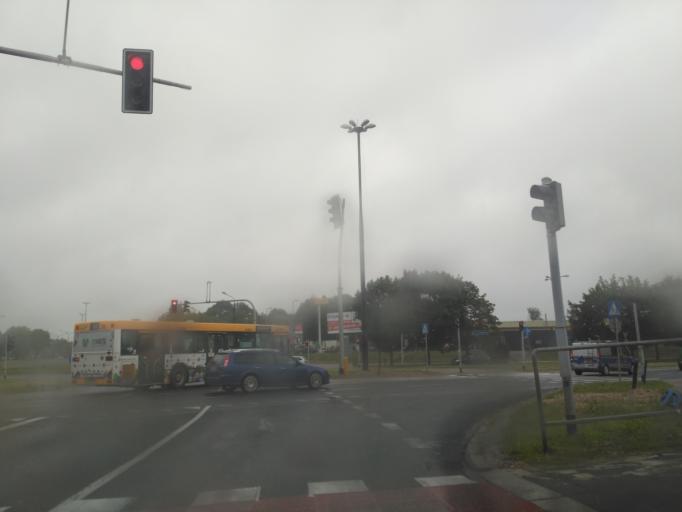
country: PL
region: Lublin Voivodeship
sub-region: Powiat lubelski
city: Lublin
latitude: 51.2689
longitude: 22.5586
